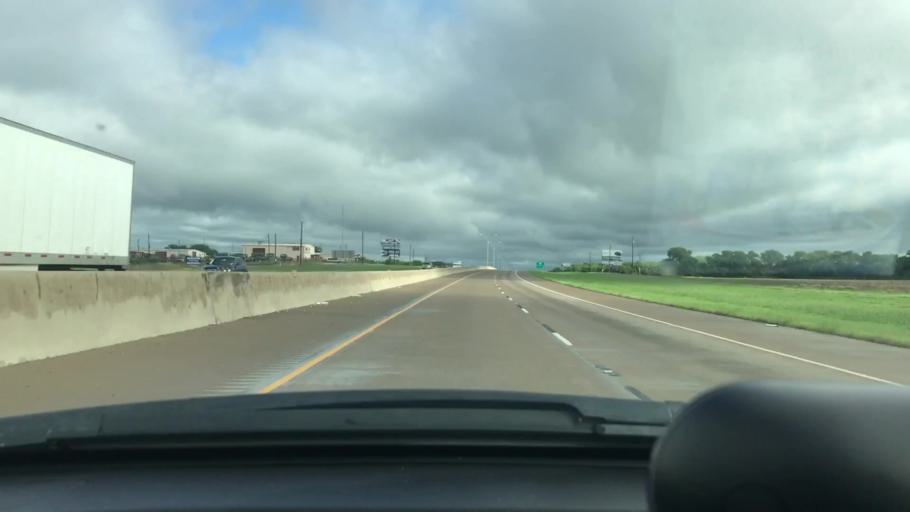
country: US
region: Texas
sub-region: Grayson County
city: Howe
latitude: 33.4834
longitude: -96.6202
